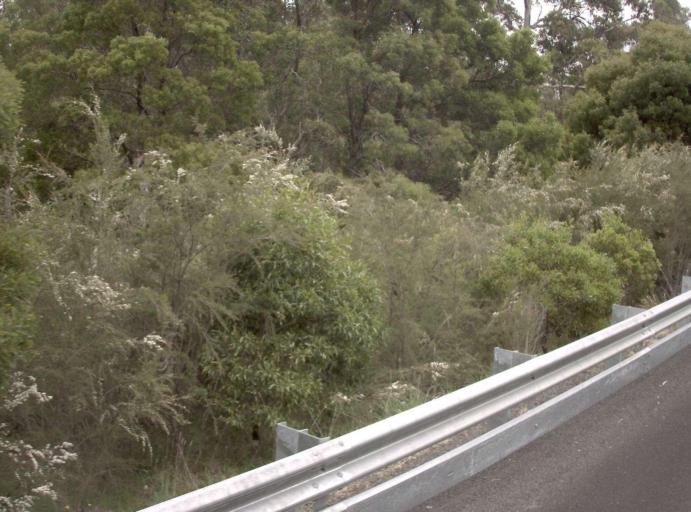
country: AU
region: New South Wales
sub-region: Bombala
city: Bombala
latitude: -37.2451
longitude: 149.2590
